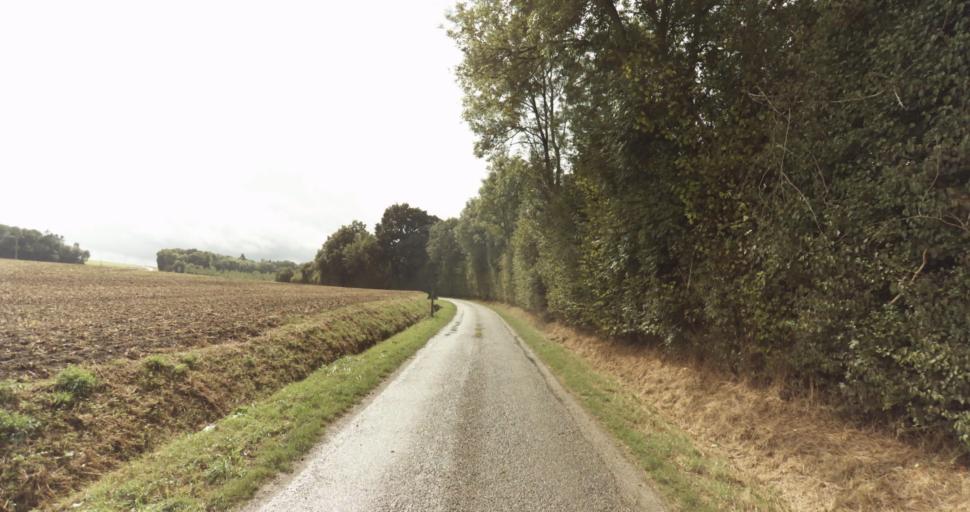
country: FR
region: Lower Normandy
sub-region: Departement de l'Orne
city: Sainte-Gauburge-Sainte-Colombe
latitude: 48.7040
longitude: 0.4090
